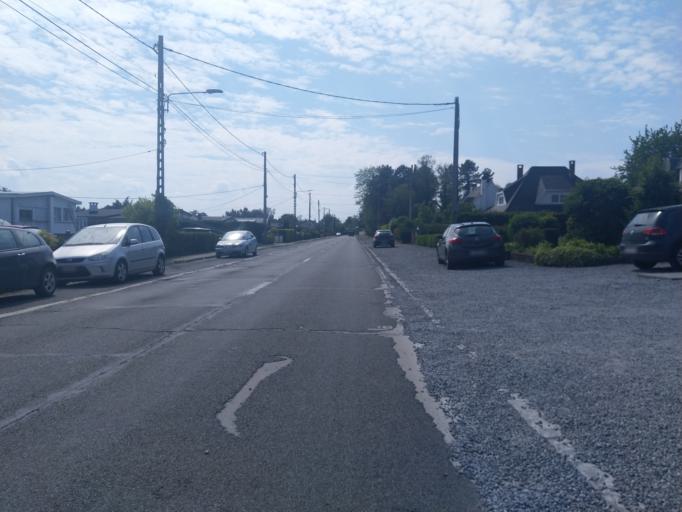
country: BE
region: Wallonia
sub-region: Province du Hainaut
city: Mons
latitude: 50.4613
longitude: 3.9943
